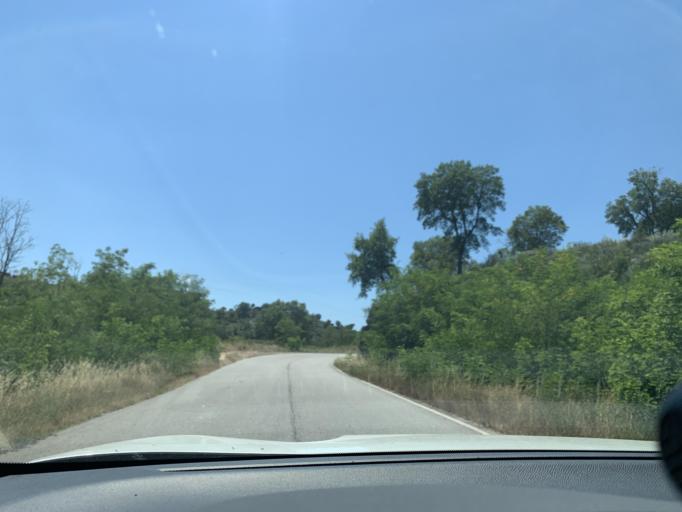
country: PT
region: Guarda
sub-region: Fornos de Algodres
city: Fornos de Algodres
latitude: 40.5696
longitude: -7.5950
